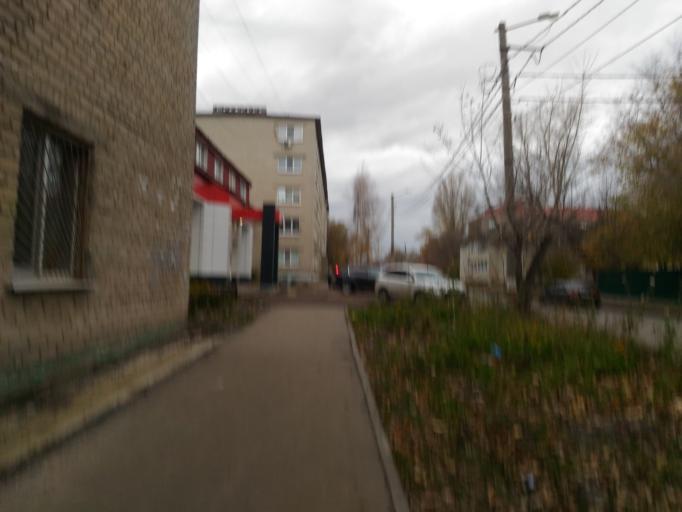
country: RU
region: Ulyanovsk
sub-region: Ulyanovskiy Rayon
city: Ulyanovsk
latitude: 54.3417
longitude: 48.3907
